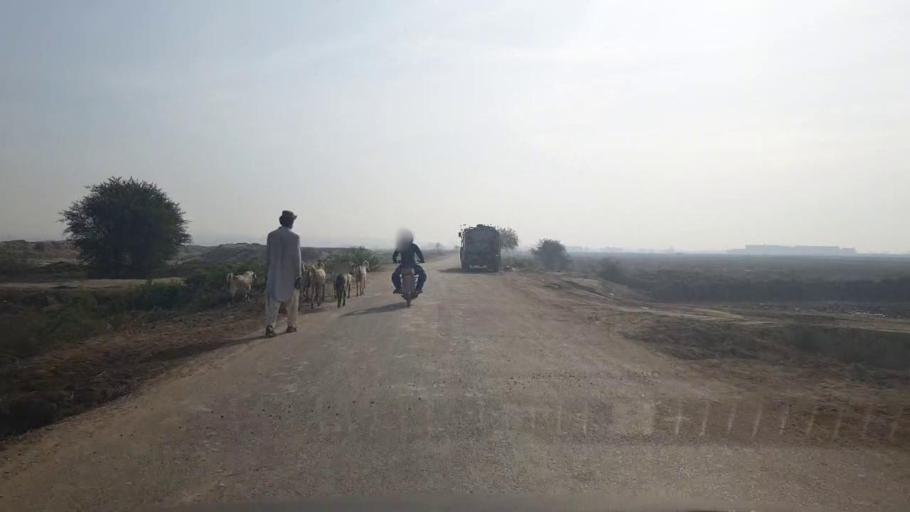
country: PK
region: Sindh
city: Umarkot
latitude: 25.3443
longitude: 69.7087
